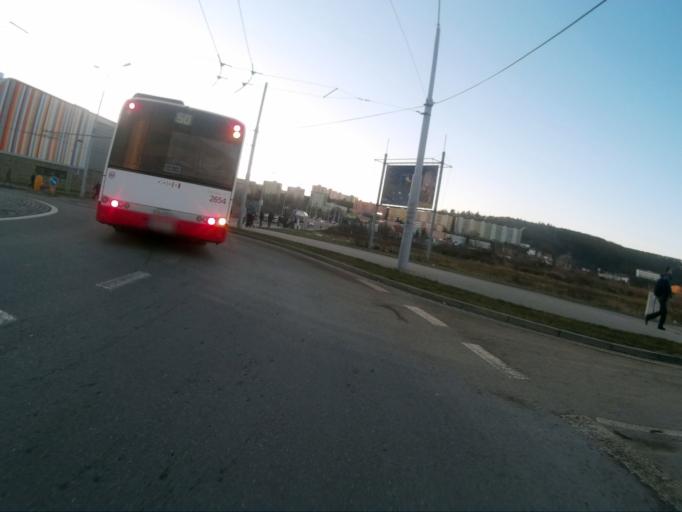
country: CZ
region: South Moravian
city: Ostopovice
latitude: 49.1782
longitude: 16.5675
